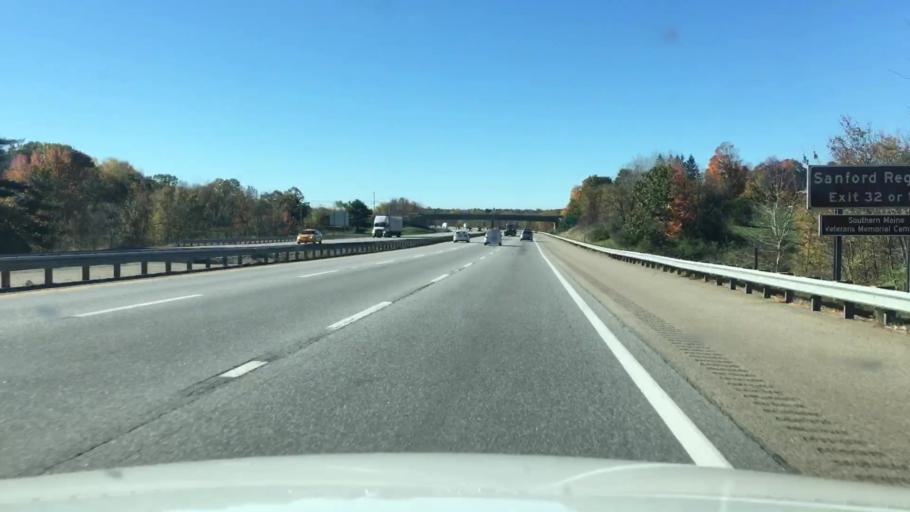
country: US
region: Maine
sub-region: York County
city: Biddeford
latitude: 43.5062
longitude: -70.4812
